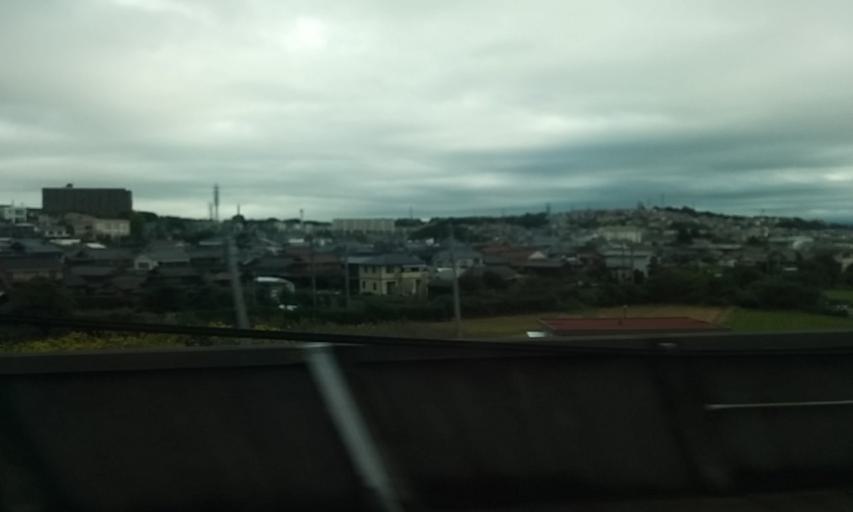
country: JP
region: Hyogo
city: Akashi
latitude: 34.6909
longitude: 134.9118
